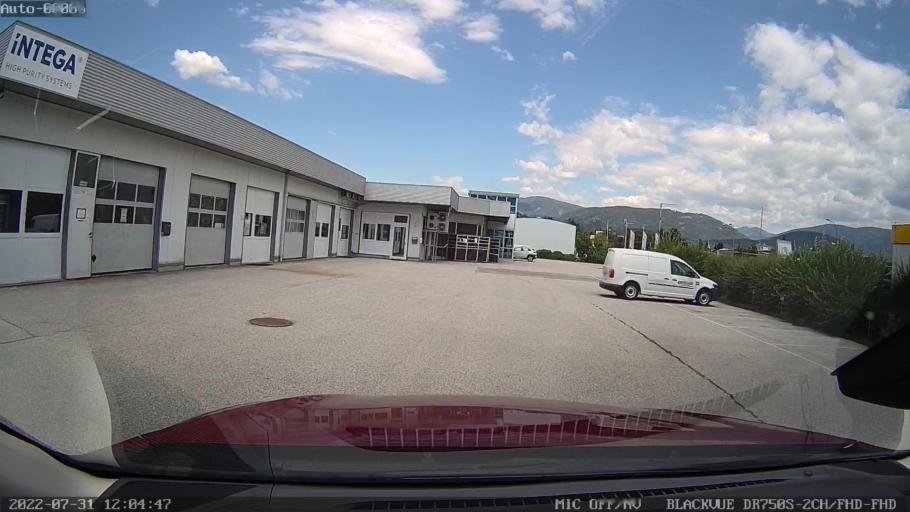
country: AT
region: Carinthia
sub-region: Villach Stadt
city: Villach
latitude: 46.5981
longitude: 13.8489
